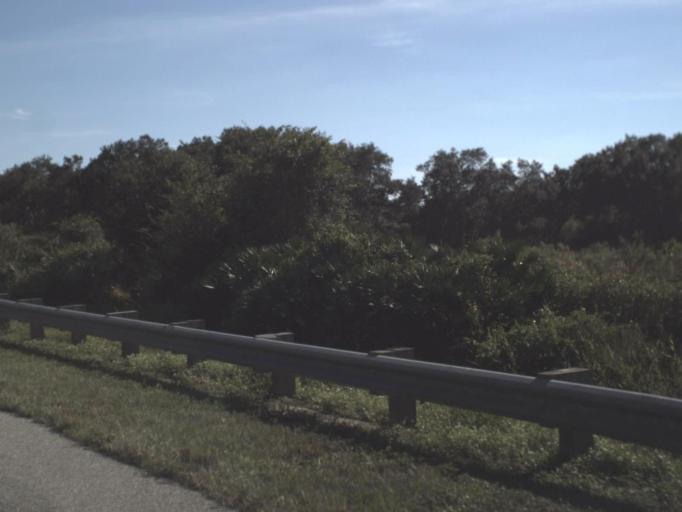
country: US
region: Florida
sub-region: Glades County
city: Moore Haven
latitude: 26.8839
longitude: -81.2301
